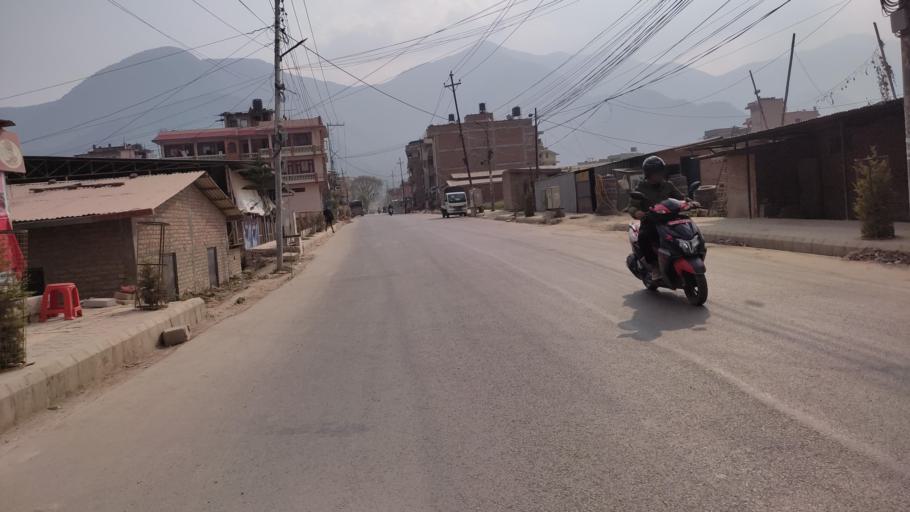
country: NP
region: Central Region
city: Kirtipur
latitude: 27.6720
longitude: 85.2727
